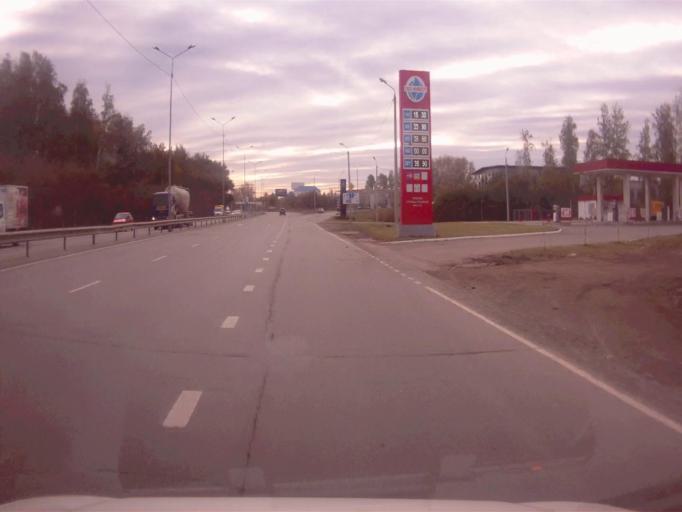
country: RU
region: Chelyabinsk
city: Novosineglazovskiy
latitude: 55.0833
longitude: 61.3940
